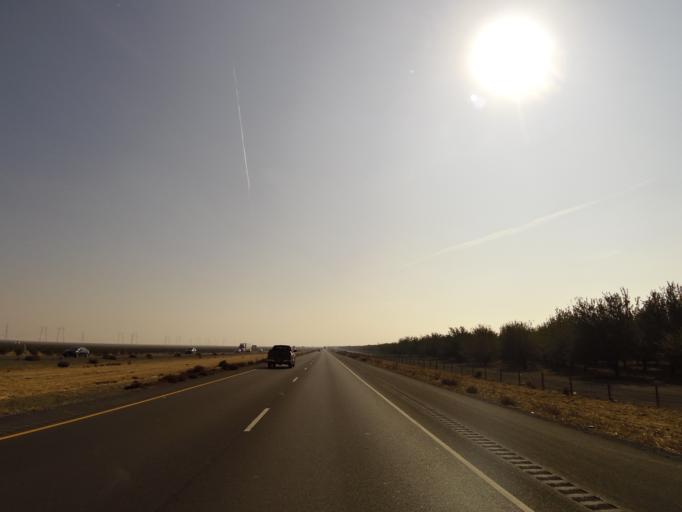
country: US
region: California
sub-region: Kings County
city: Kettleman City
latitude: 35.9280
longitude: -119.9056
